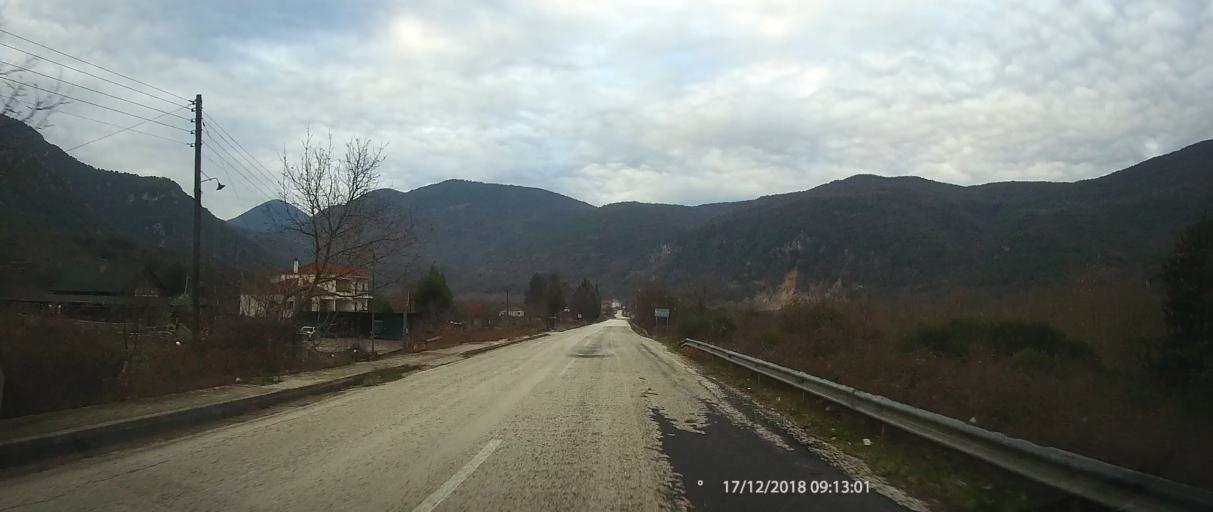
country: GR
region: Epirus
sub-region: Nomos Ioanninon
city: Kalpaki
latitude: 39.9761
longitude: 20.6625
